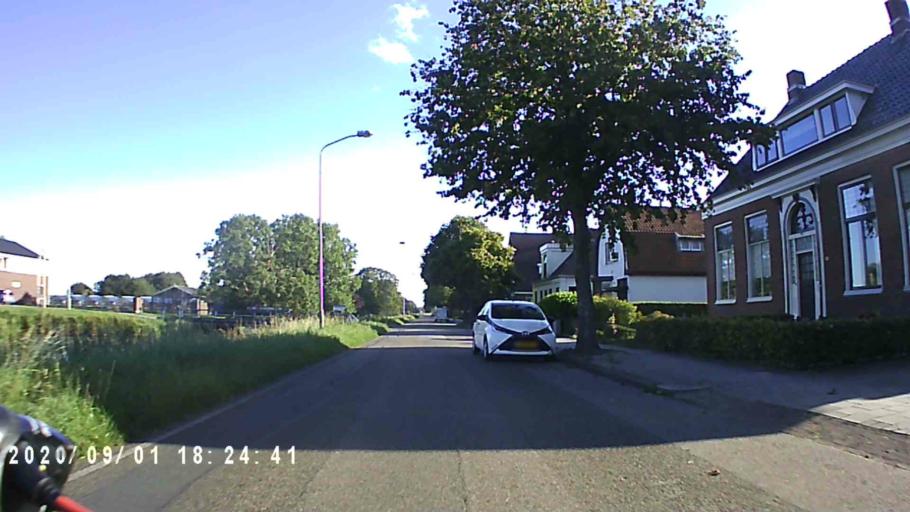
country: NL
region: Groningen
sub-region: Gemeente Hoogezand-Sappemeer
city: Sappemeer
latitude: 53.1618
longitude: 6.7960
